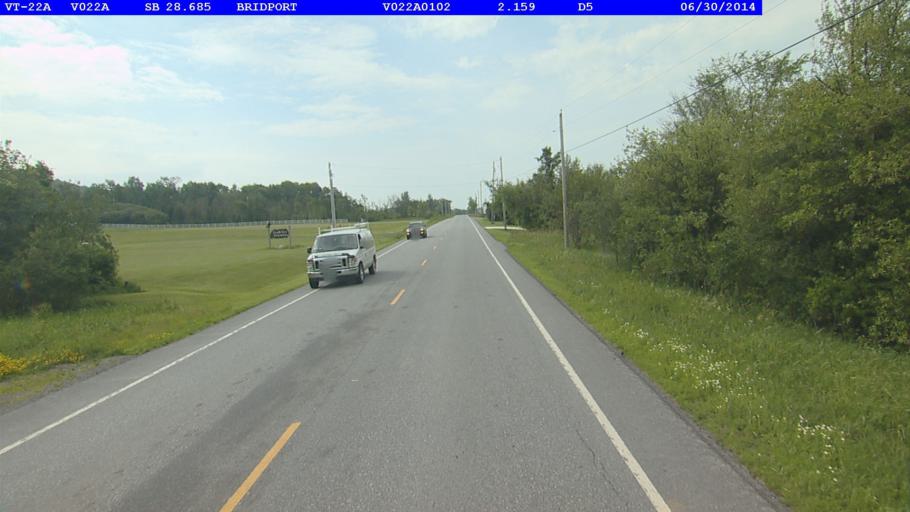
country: US
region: Vermont
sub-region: Addison County
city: Middlebury (village)
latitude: 43.9713
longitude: -73.3107
